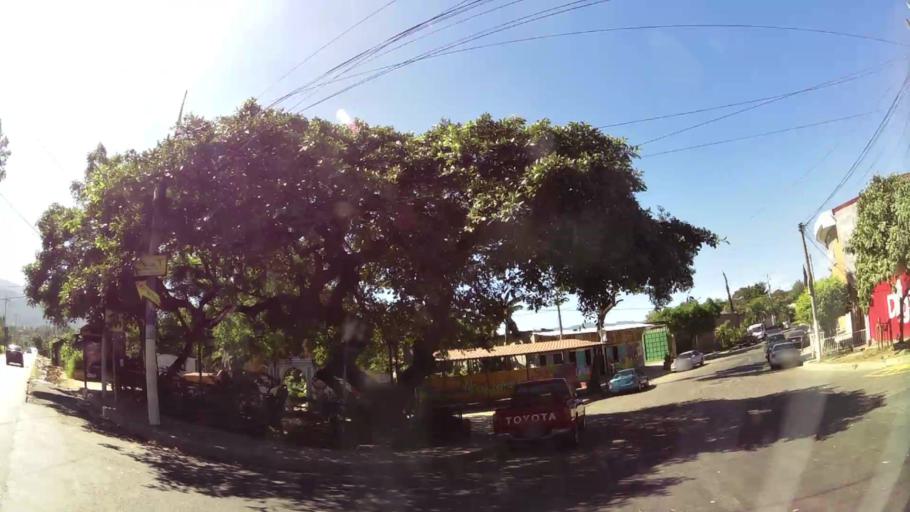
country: SV
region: Ahuachapan
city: Ahuachapan
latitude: 13.9195
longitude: -89.8405
